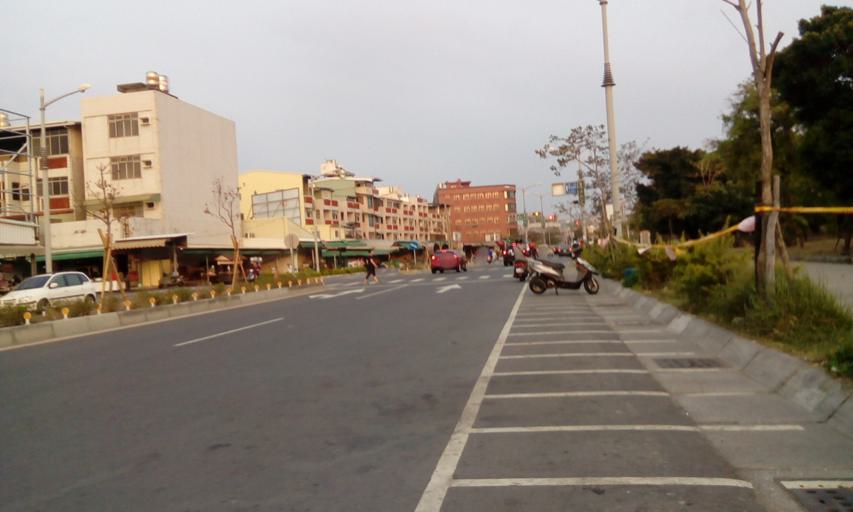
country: TW
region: Kaohsiung
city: Kaohsiung
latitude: 22.6900
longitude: 120.2991
